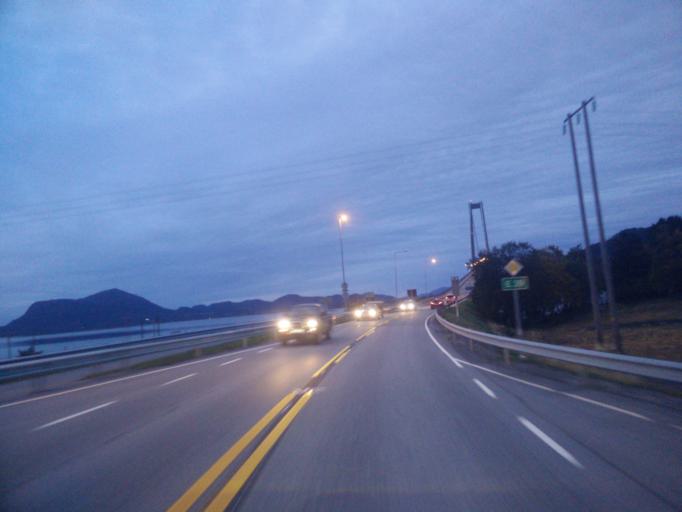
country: NO
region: More og Romsdal
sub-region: Gjemnes
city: Batnfjordsora
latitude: 62.9646
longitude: 7.7692
